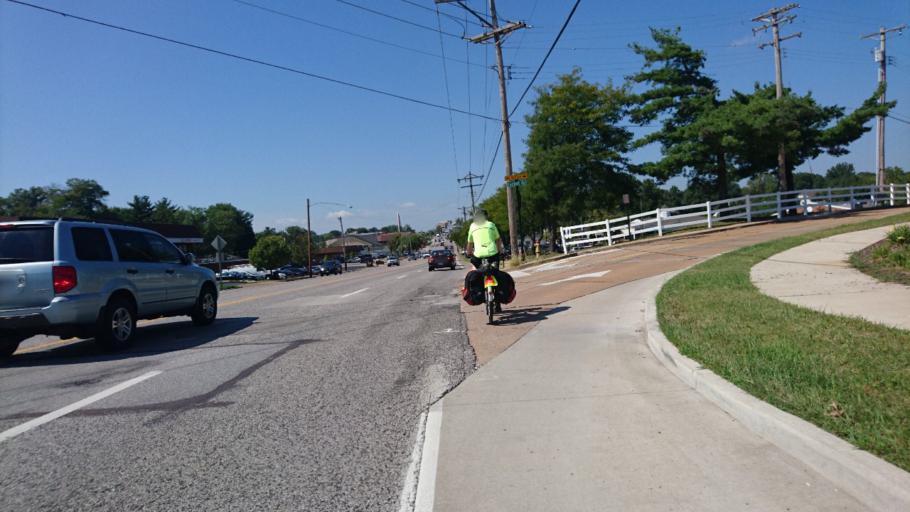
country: US
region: Missouri
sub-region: Saint Louis County
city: Des Peres
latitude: 38.6002
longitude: -90.4276
